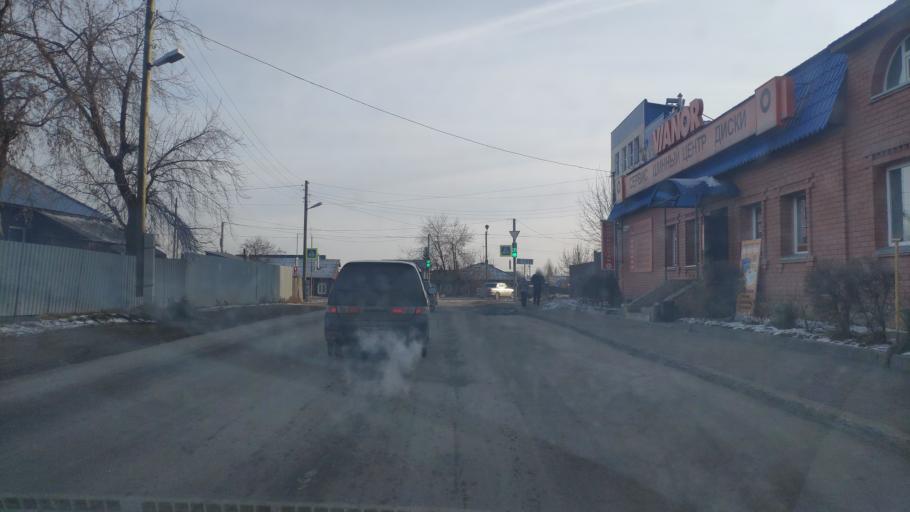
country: RU
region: Kurgan
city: Shadrinsk
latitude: 56.0880
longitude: 63.6722
